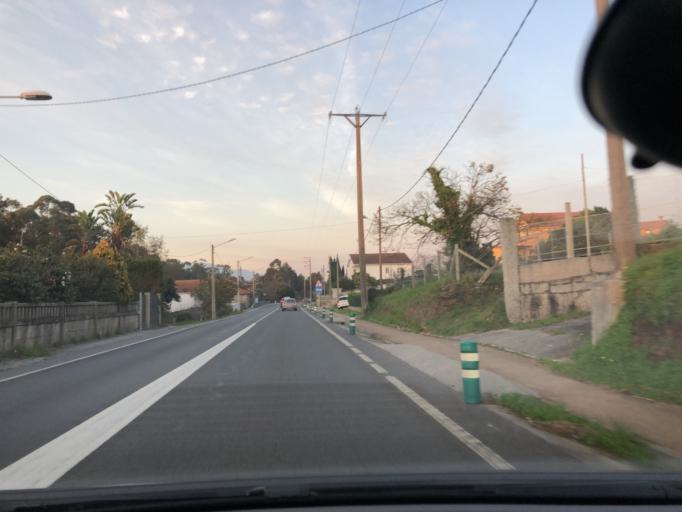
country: ES
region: Galicia
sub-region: Provincia de Pontevedra
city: Marin
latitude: 42.3813
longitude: -8.7235
